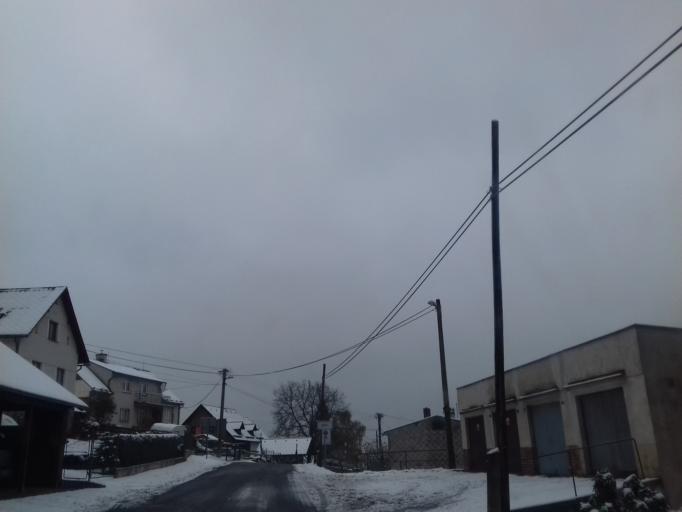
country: CZ
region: Plzensky
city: Postrekov
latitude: 49.4432
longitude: 12.7853
